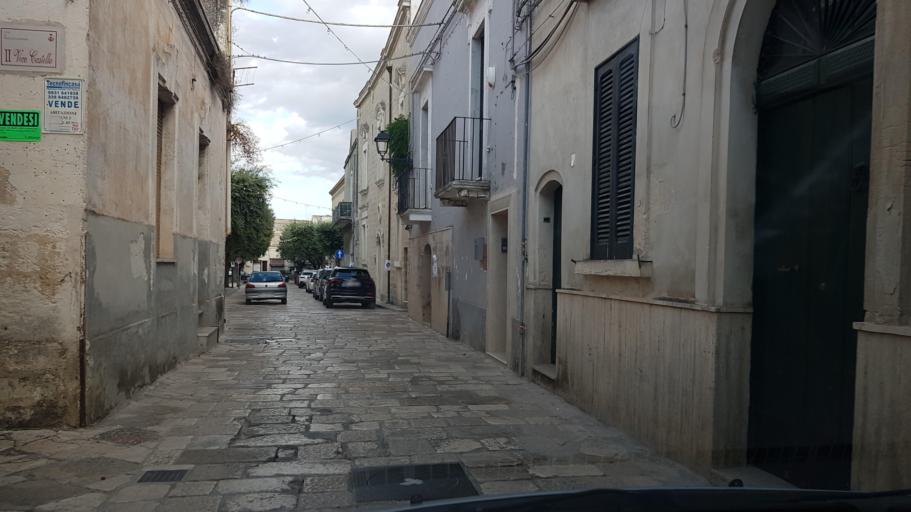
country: IT
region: Apulia
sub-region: Provincia di Brindisi
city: Francavilla Fontana
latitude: 40.5324
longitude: 17.5830
